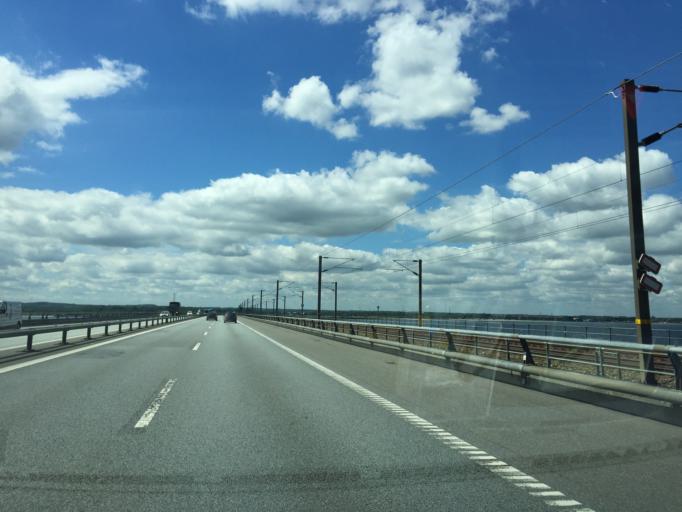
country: DK
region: South Denmark
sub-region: Nyborg Kommune
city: Nyborg
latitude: 55.3024
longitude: 10.8673
